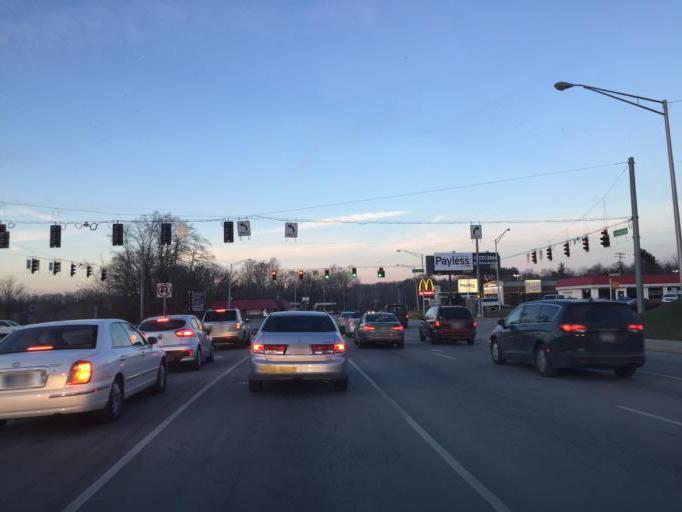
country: US
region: Indiana
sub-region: Monroe County
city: Bloomington
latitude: 39.1858
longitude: -86.5345
